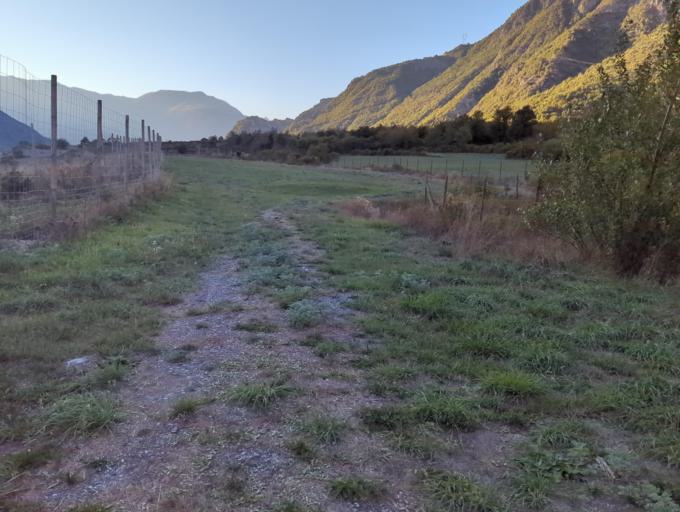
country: FR
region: Rhone-Alpes
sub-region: Departement de la Savoie
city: Saint-Michel-de-Maurienne
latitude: 45.2476
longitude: 6.4267
